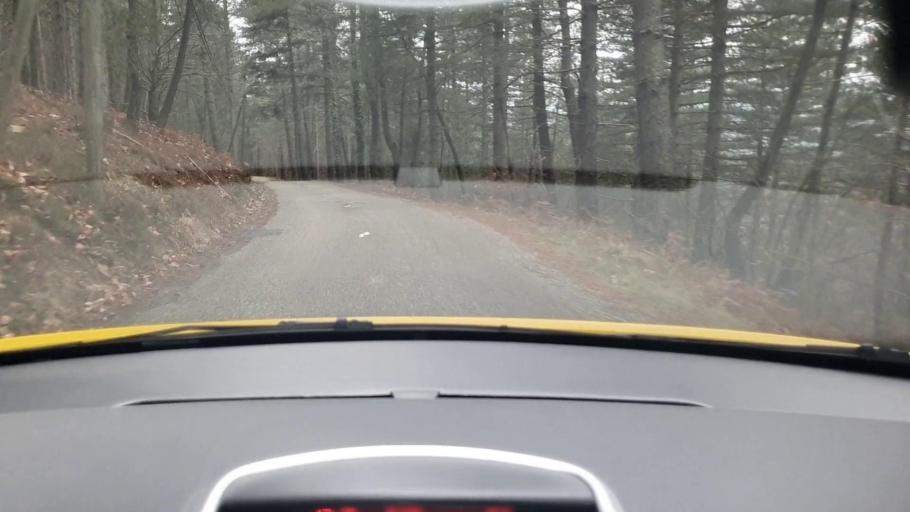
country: FR
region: Languedoc-Roussillon
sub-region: Departement du Gard
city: Besseges
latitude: 44.3555
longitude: 4.0205
